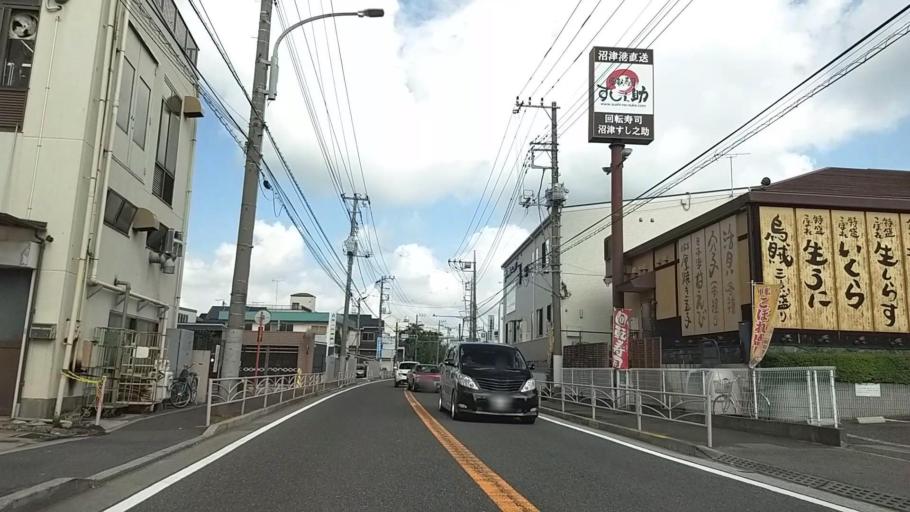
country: JP
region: Kanagawa
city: Minami-rinkan
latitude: 35.4846
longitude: 139.5237
